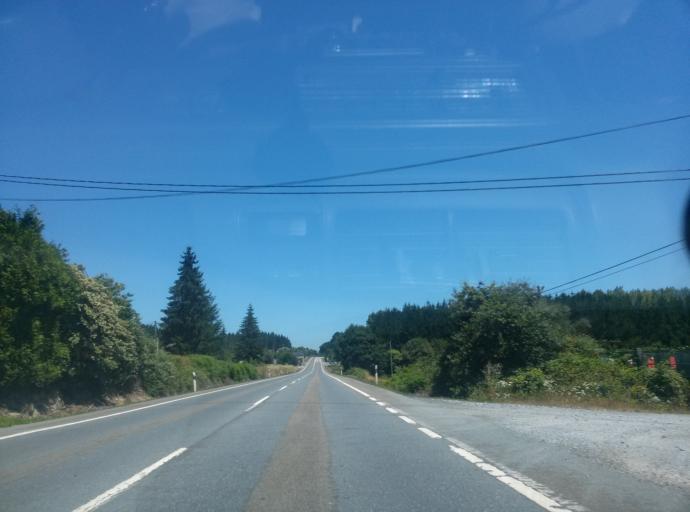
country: ES
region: Galicia
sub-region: Provincia de Lugo
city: Lugo
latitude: 43.0793
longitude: -7.4861
